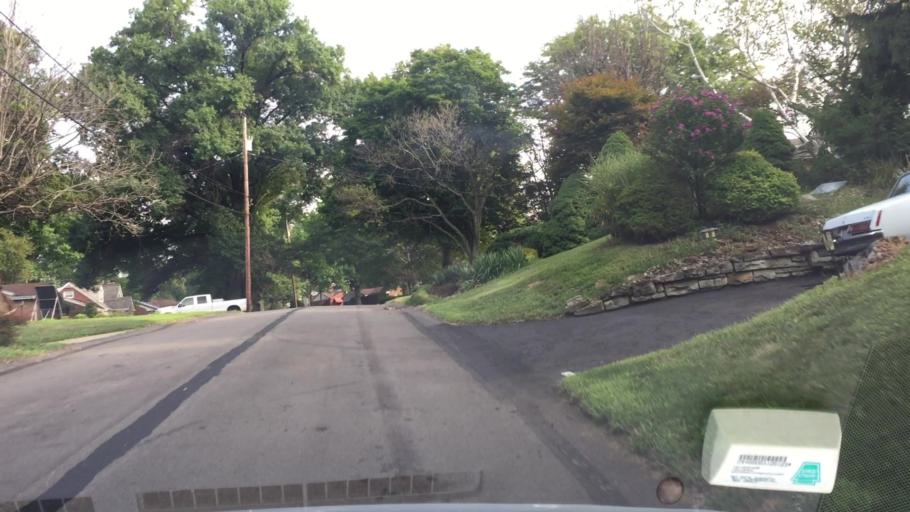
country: US
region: Pennsylvania
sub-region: Allegheny County
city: Mount Lebanon
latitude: 40.3622
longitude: -80.0727
